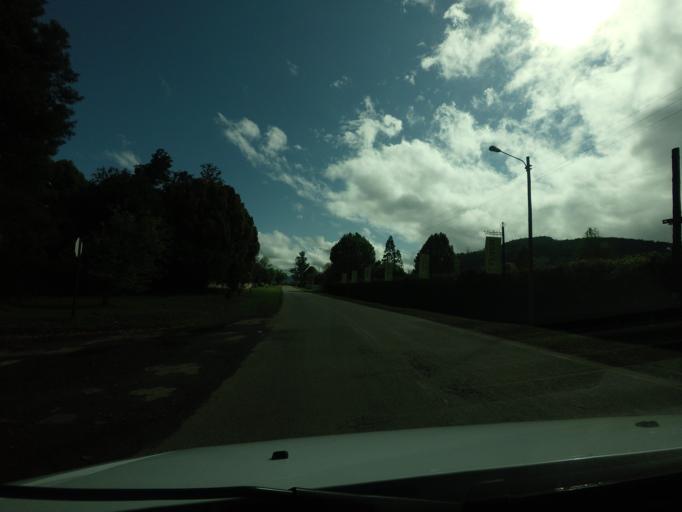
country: ZA
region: Mpumalanga
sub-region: Ehlanzeni District
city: Graksop
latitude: -25.0917
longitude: 30.7747
